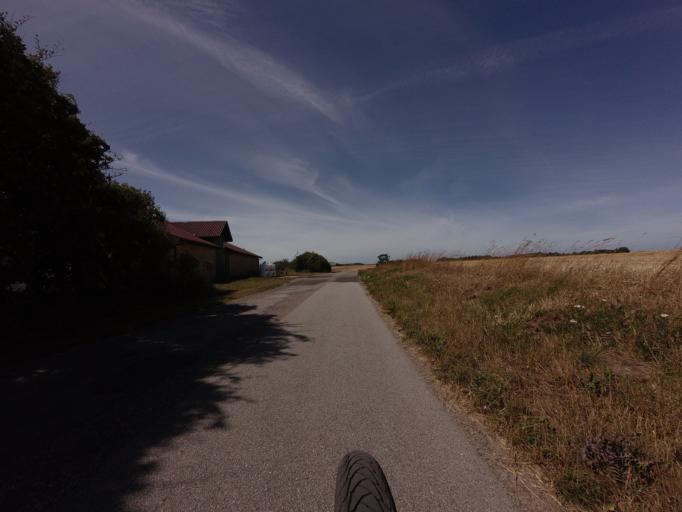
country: DK
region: North Denmark
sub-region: Jammerbugt Kommune
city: Pandrup
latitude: 57.3795
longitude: 9.7613
